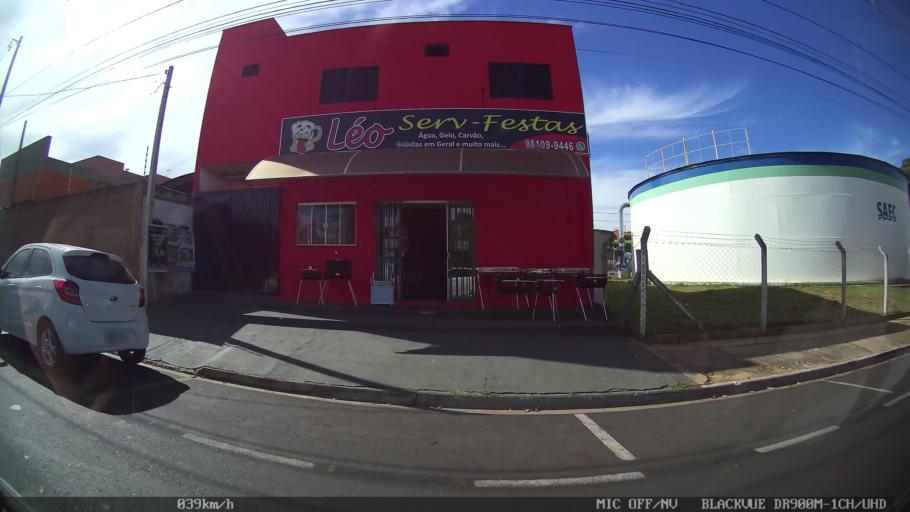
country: BR
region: Sao Paulo
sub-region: Catanduva
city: Catanduva
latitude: -21.1261
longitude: -48.9604
